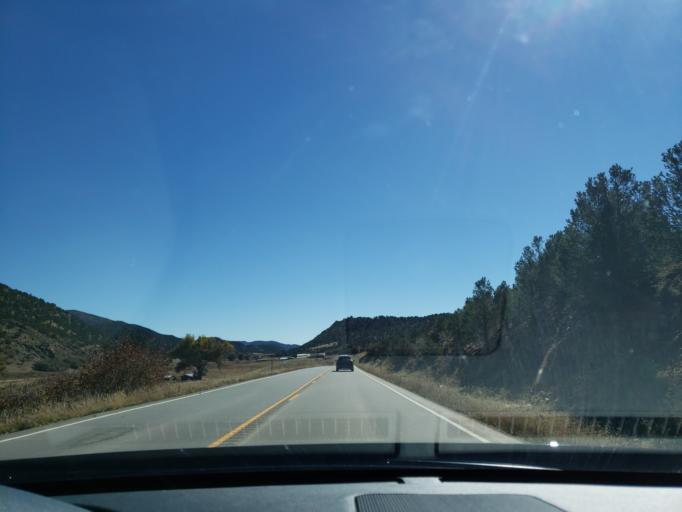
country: US
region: Colorado
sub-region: Fremont County
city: Canon City
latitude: 38.6098
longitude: -105.4399
